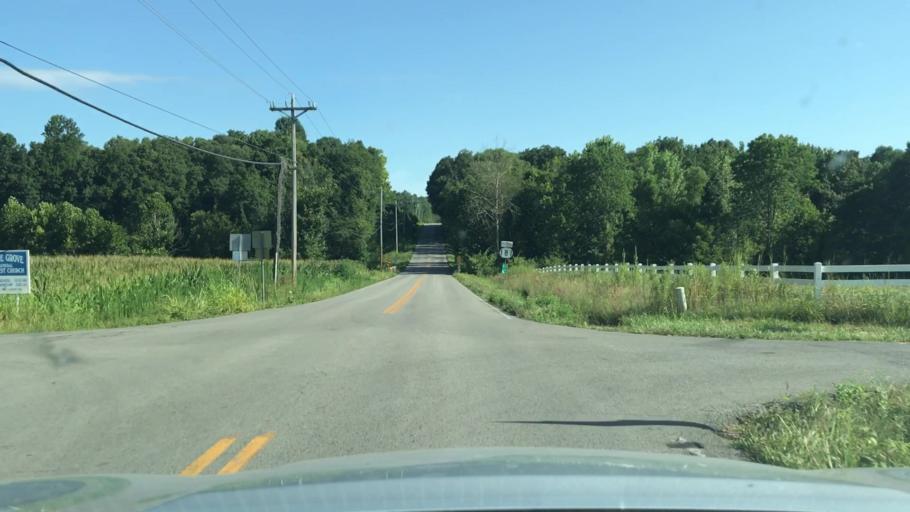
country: US
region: Kentucky
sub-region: Muhlenberg County
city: Greenville
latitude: 37.1016
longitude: -87.1265
